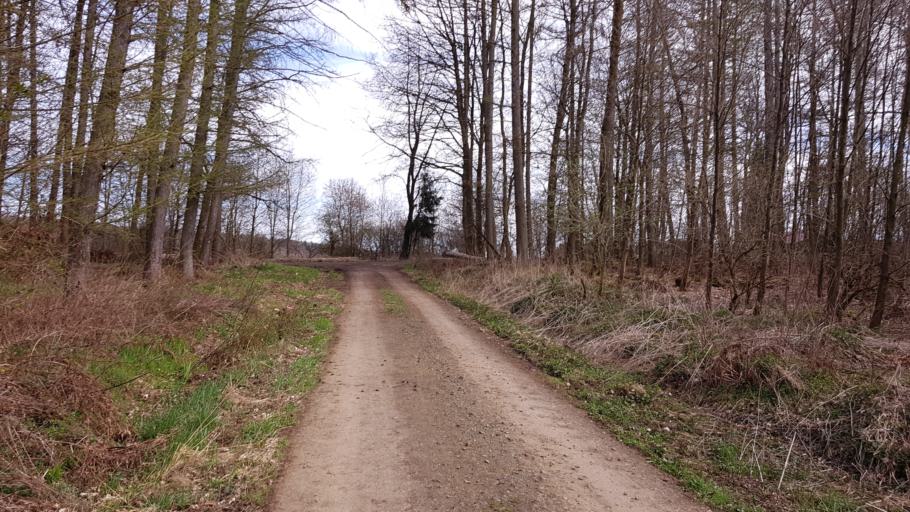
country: DE
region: Hesse
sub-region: Regierungsbezirk Giessen
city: Homberg
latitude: 50.6600
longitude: 9.0473
